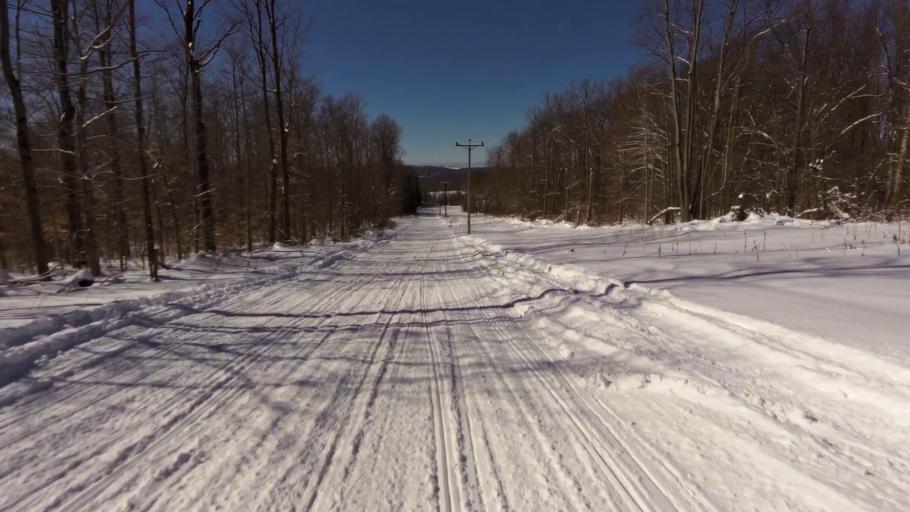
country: US
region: New York
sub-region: Chautauqua County
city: Mayville
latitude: 42.2751
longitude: -79.4584
